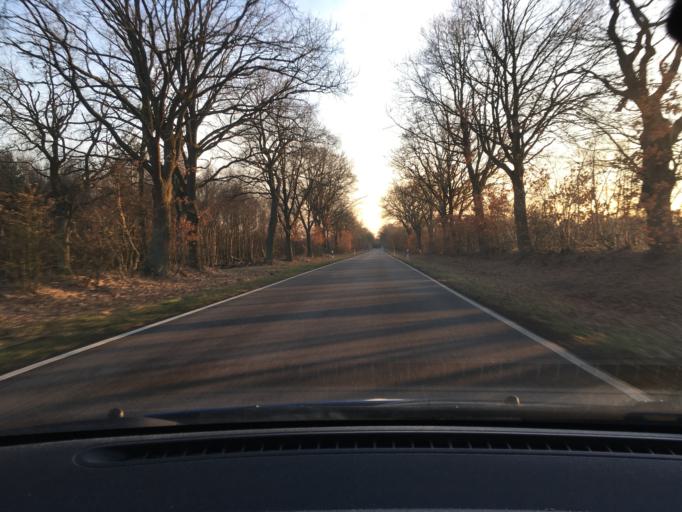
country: DE
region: Schleswig-Holstein
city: Langenlehsten
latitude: 53.5106
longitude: 10.7432
